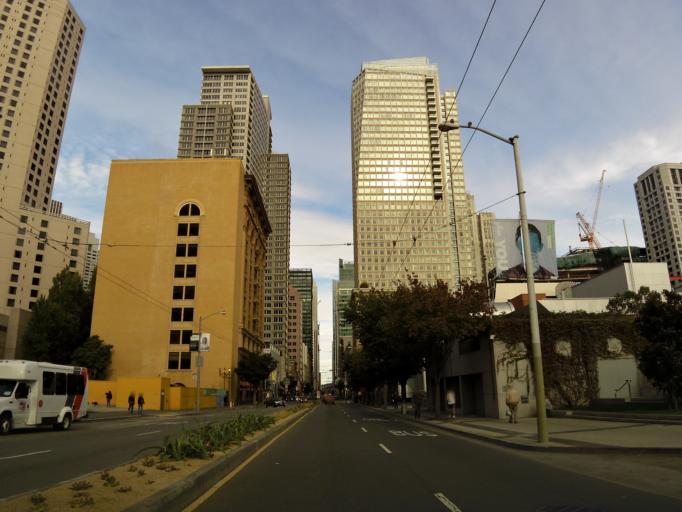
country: US
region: California
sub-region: San Francisco County
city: San Francisco
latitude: 37.7853
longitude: -122.4032
